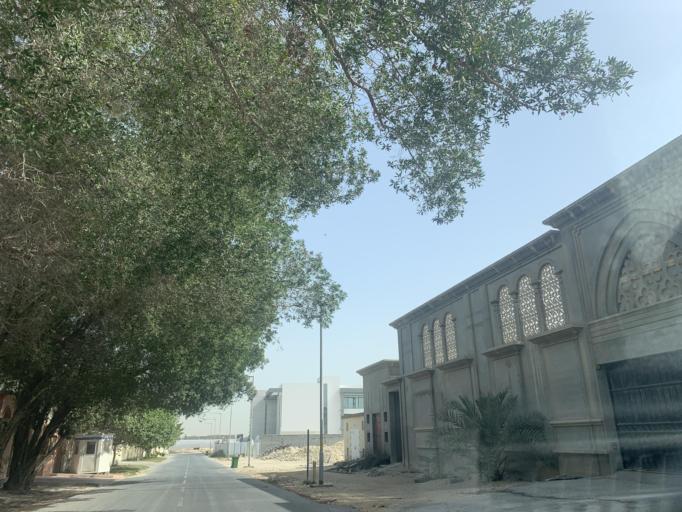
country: BH
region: Northern
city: Ar Rifa'
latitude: 26.1424
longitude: 50.5367
